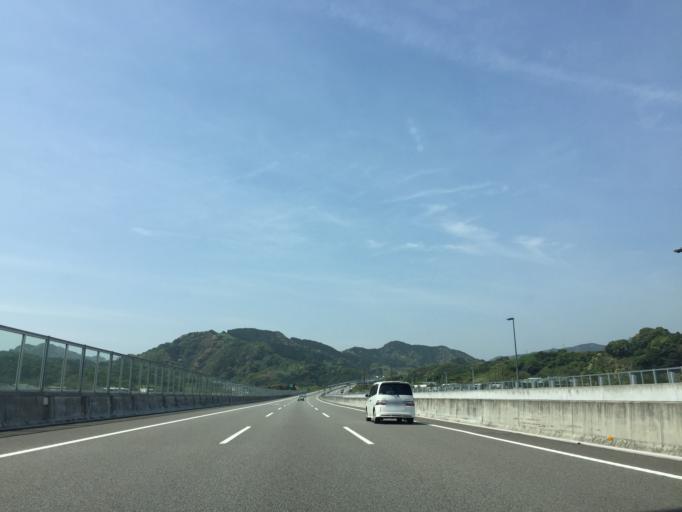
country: JP
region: Shizuoka
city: Fujieda
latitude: 34.9046
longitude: 138.2485
